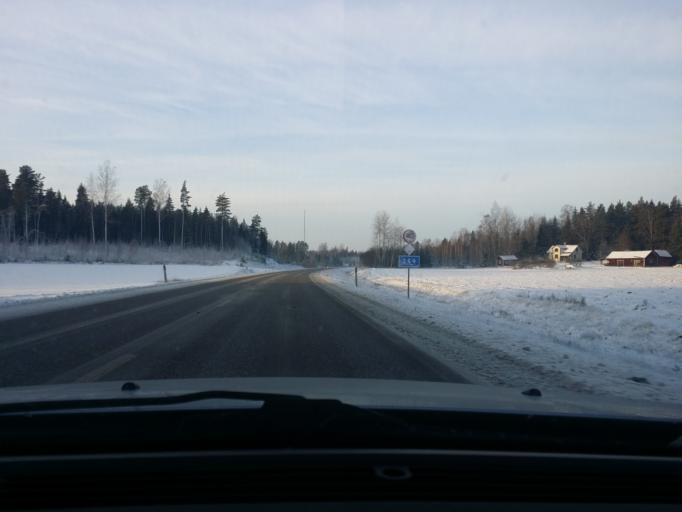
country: SE
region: OErebro
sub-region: Lindesbergs Kommun
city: Frovi
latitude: 59.4585
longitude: 15.4515
